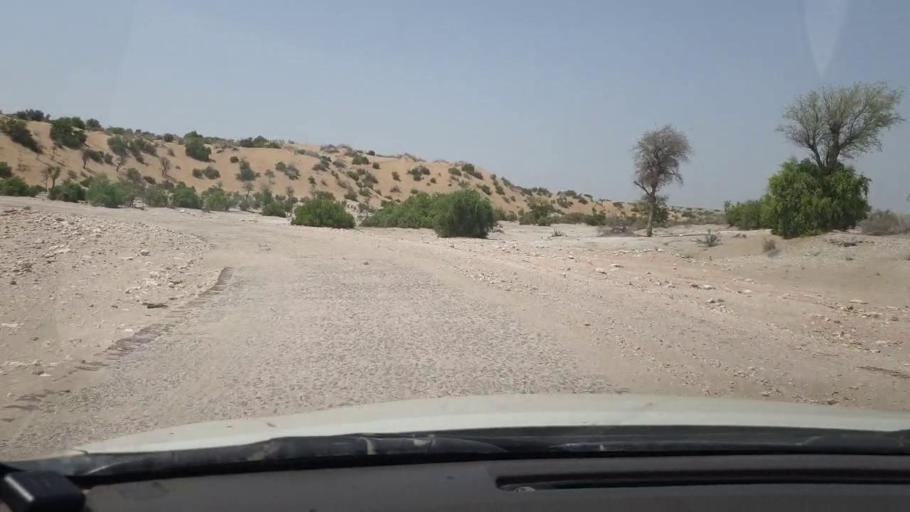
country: PK
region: Sindh
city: Rohri
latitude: 27.3235
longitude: 69.2770
